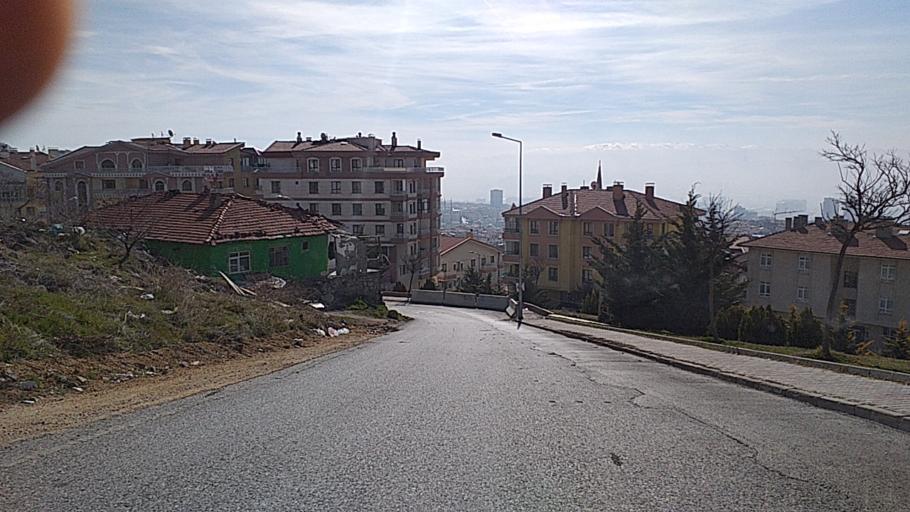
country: TR
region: Ankara
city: Ankara
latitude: 39.9895
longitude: 32.8134
